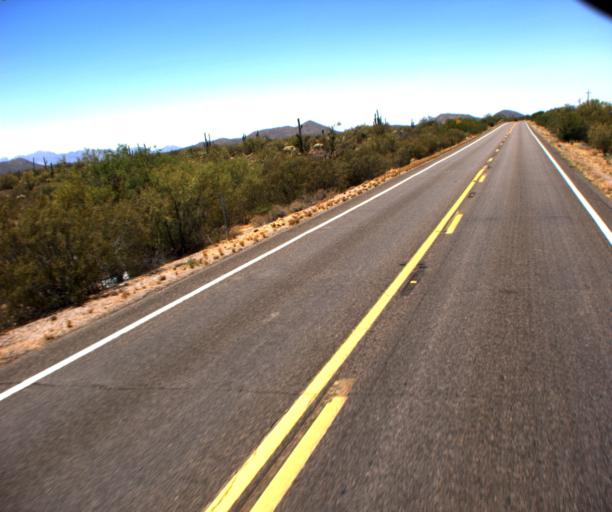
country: US
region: Arizona
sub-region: Pima County
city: Catalina
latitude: 32.7024
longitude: -111.0930
